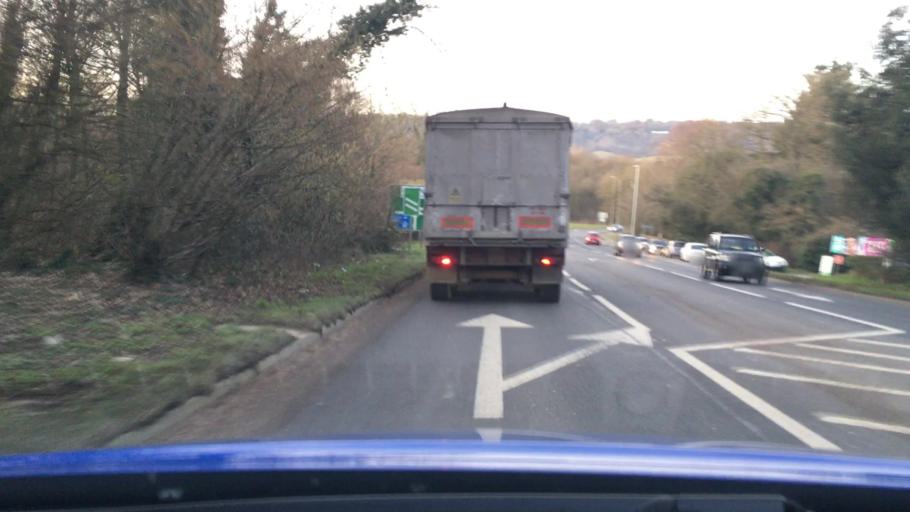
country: GB
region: England
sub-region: Kent
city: Borough Green
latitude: 51.3000
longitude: 0.3377
